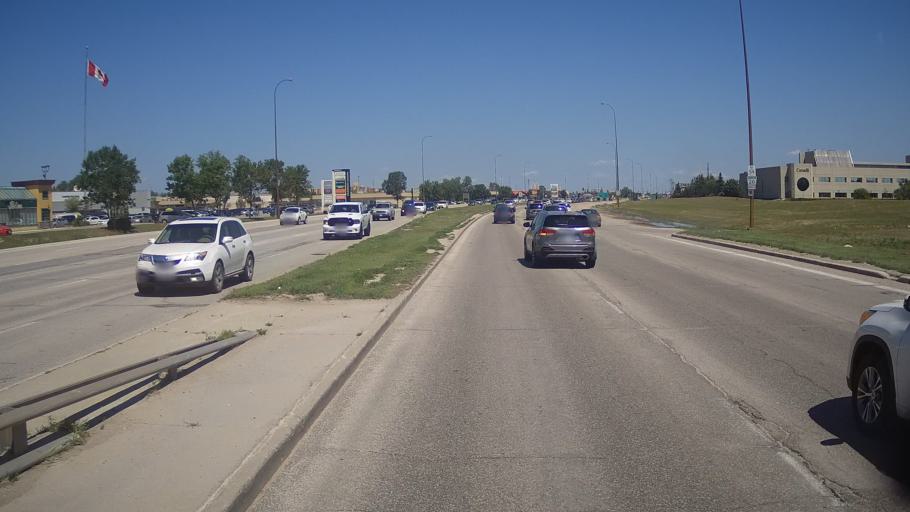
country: CA
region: Manitoba
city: Winnipeg
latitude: 49.8990
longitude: -97.0687
